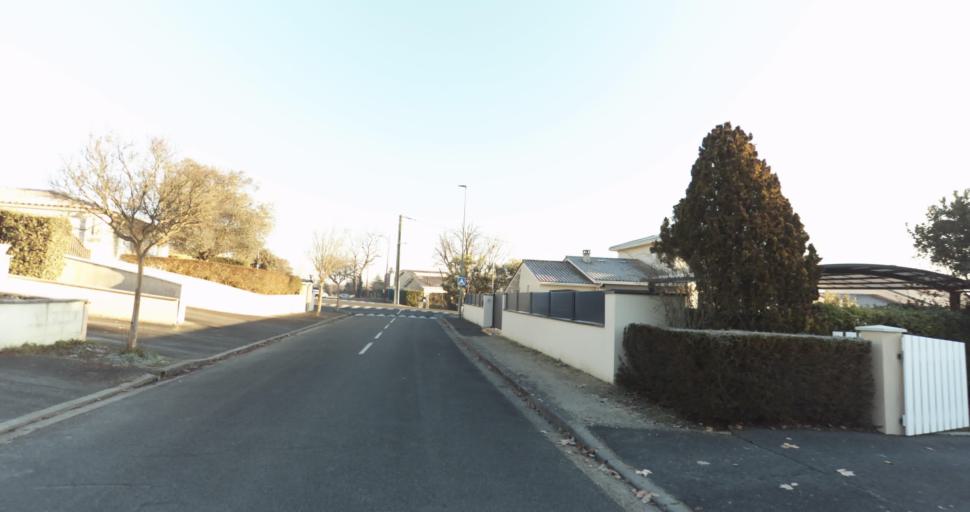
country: FR
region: Aquitaine
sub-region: Departement de la Gironde
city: Carbon-Blanc
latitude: 44.9095
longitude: -0.4996
